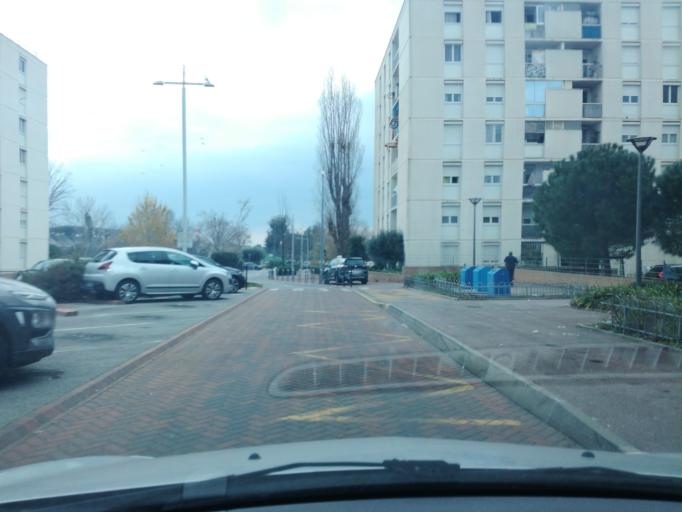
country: FR
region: Provence-Alpes-Cote d'Azur
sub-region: Departement des Alpes-Maritimes
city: Mandelieu-la-Napoule
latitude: 43.5567
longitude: 6.9629
